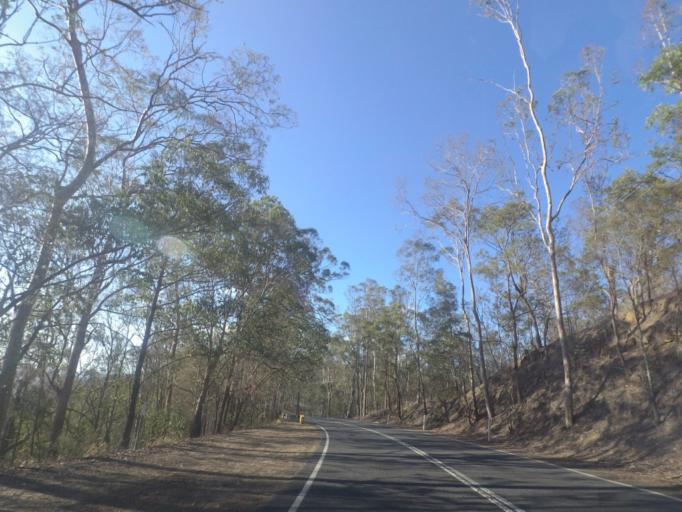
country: AU
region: Queensland
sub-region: Brisbane
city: Taringa
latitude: -27.4837
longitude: 152.9553
